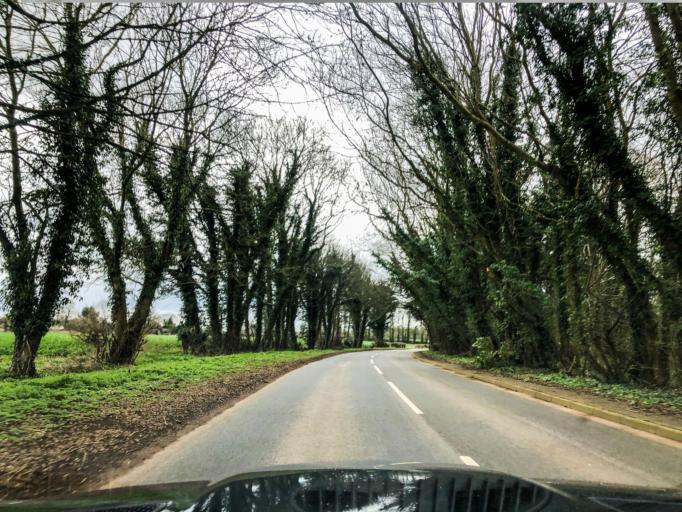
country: GB
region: England
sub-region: Oxfordshire
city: Hanwell
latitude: 52.1288
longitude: -1.4465
